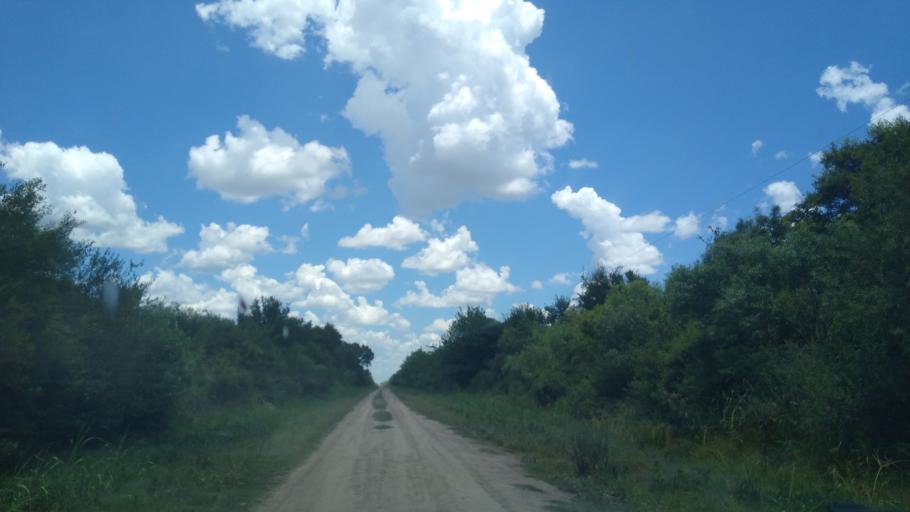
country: AR
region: Chaco
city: Presidencia Roque Saenz Pena
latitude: -26.7482
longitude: -60.3368
